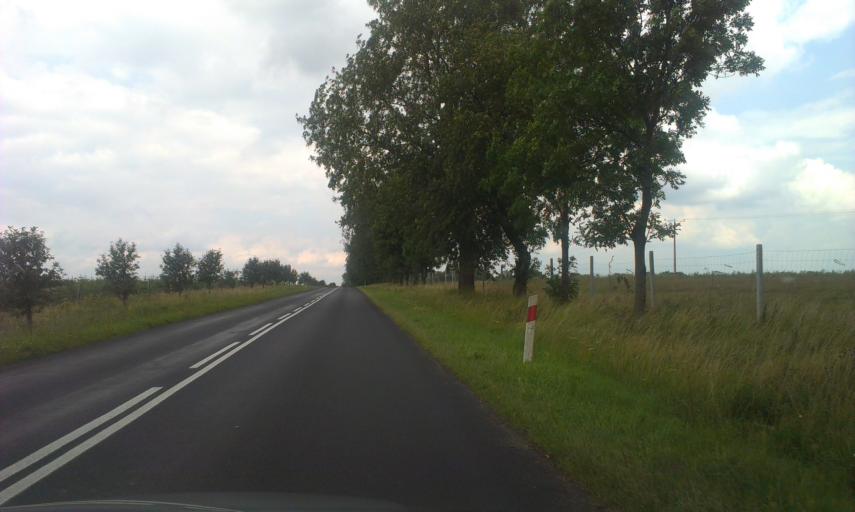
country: PL
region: West Pomeranian Voivodeship
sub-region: Powiat swidwinski
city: Polczyn-Zdroj
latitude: 53.8648
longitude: 16.0703
